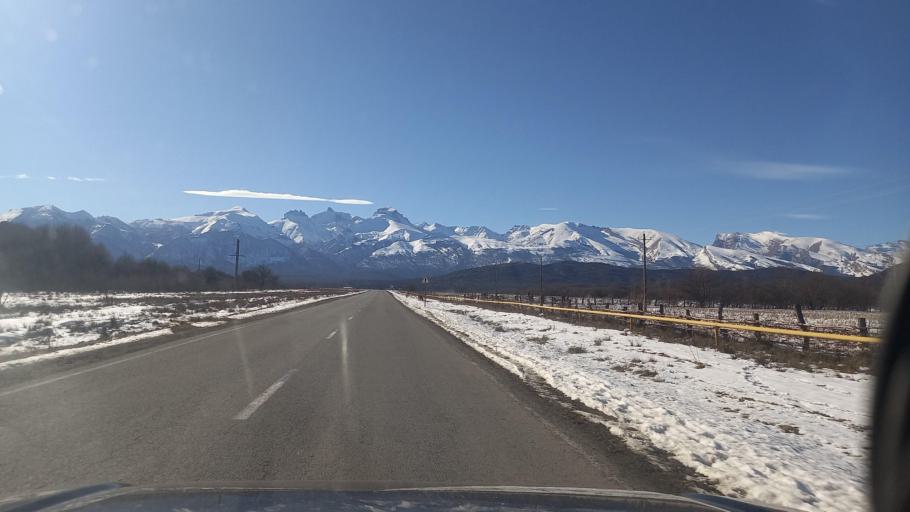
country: RU
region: North Ossetia
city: Chikola
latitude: 43.1463
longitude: 43.8333
